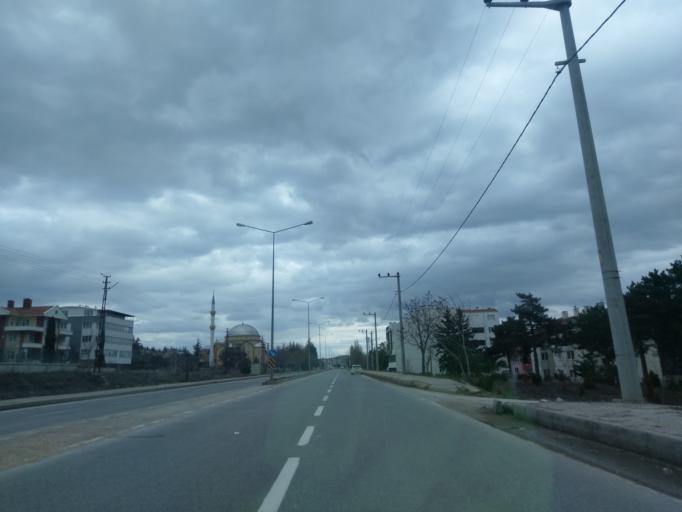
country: TR
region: Eskisehir
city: Eskisehir
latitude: 39.7457
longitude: 30.4461
